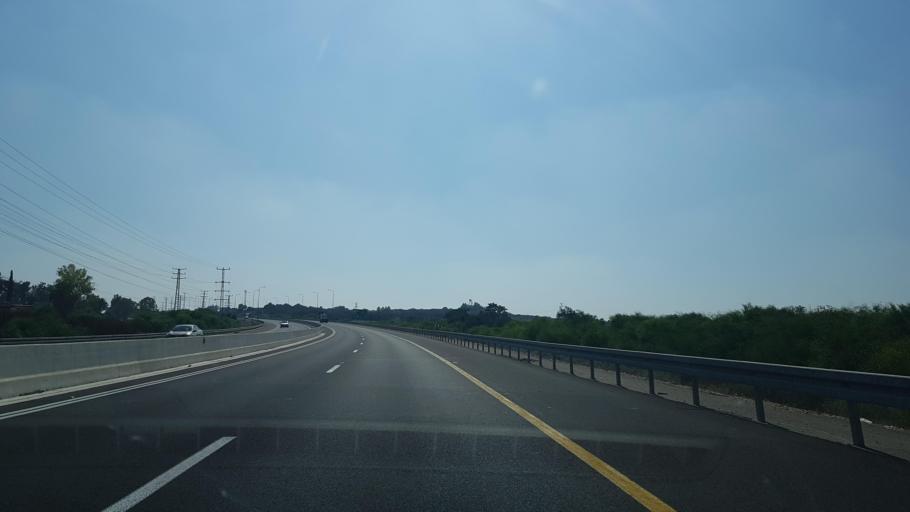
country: IL
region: Central District
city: Gan Yavne
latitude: 31.6891
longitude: 34.6735
